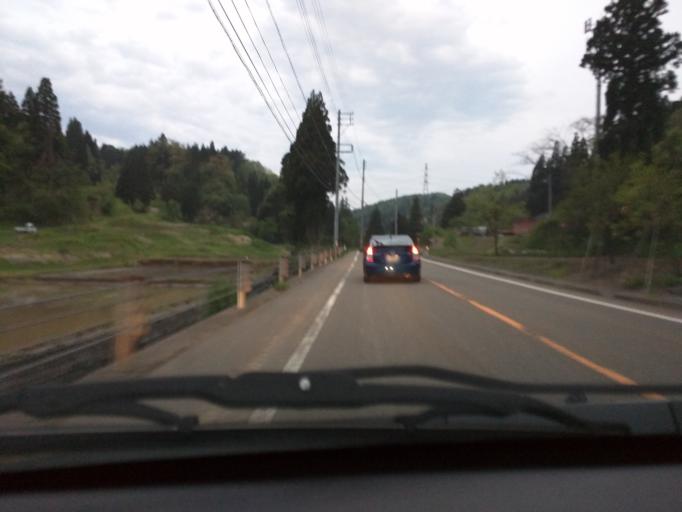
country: JP
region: Niigata
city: Ojiya
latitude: 37.3191
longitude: 138.6992
